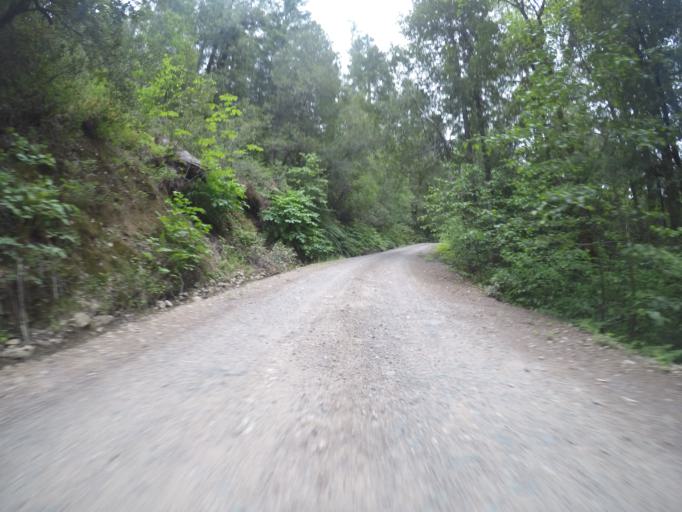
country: US
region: California
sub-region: Del Norte County
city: Bertsch-Oceanview
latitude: 41.7421
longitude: -123.8793
